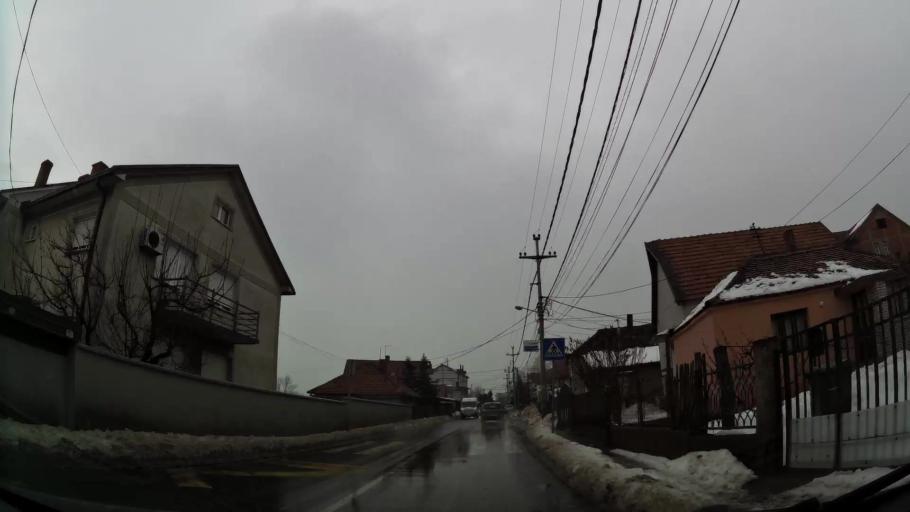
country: RS
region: Central Serbia
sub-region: Belgrade
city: Zvezdara
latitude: 44.7713
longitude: 20.5356
